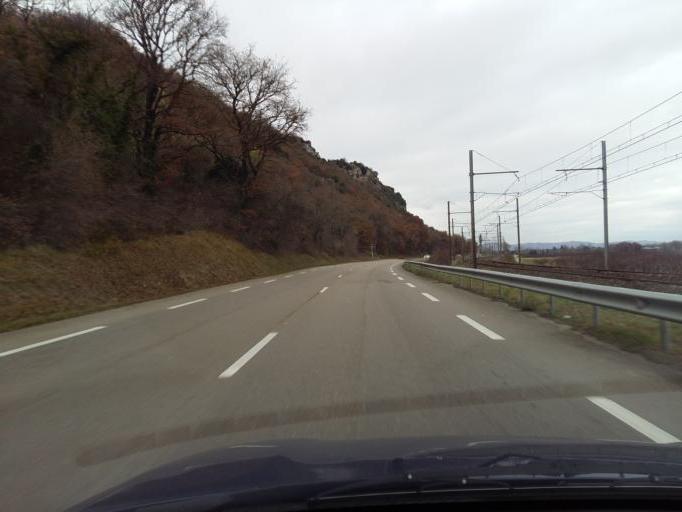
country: FR
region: Rhone-Alpes
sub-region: Departement de l'Ardeche
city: Cornas
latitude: 44.9858
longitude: 4.8478
